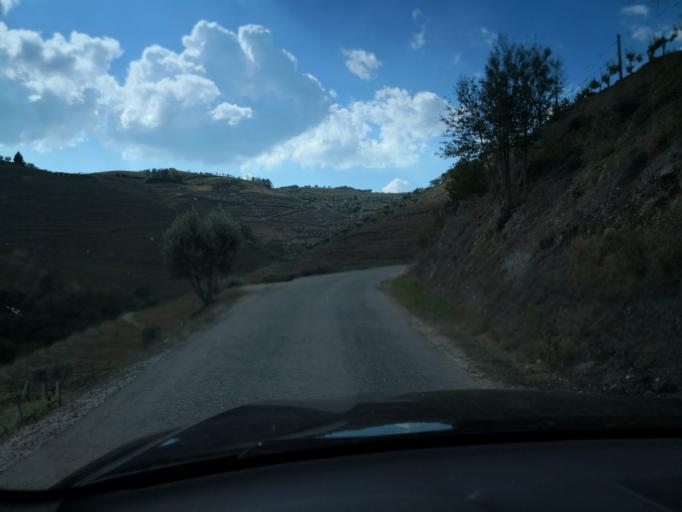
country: PT
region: Vila Real
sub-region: Sabrosa
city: Vilela
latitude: 41.1994
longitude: -7.6570
